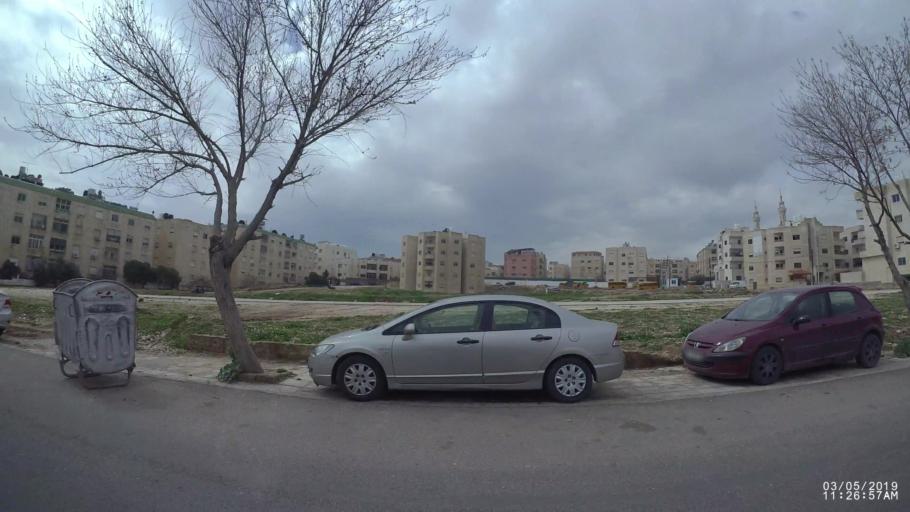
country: JO
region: Amman
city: Amman
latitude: 31.9888
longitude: 35.9311
